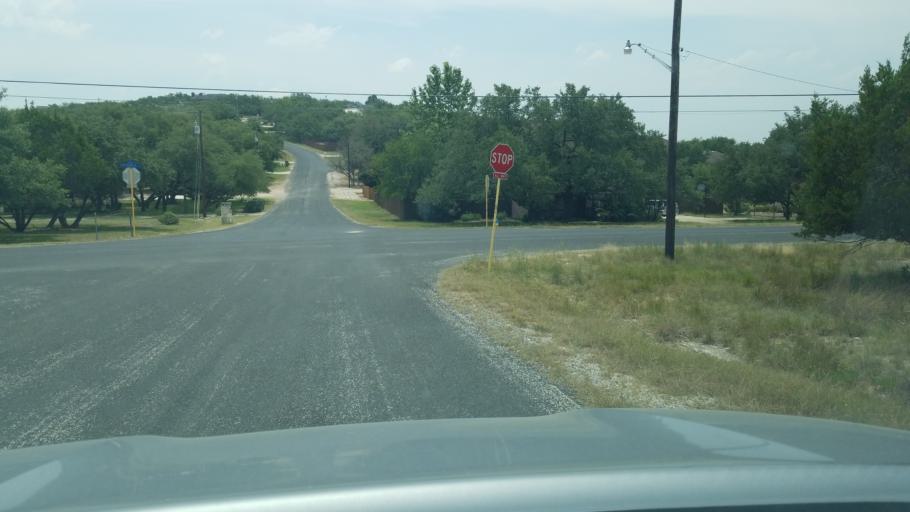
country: US
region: Texas
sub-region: Bexar County
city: Timberwood Park
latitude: 29.6891
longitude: -98.4958
